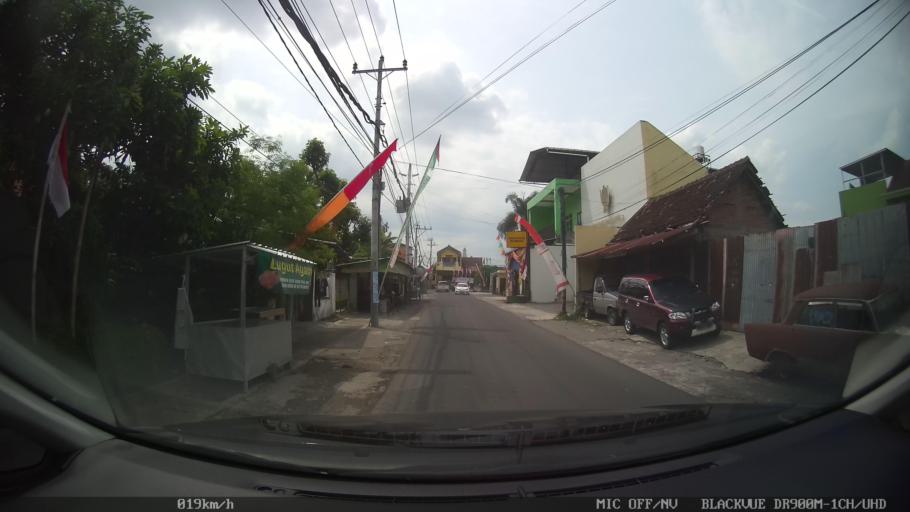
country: ID
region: Daerah Istimewa Yogyakarta
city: Yogyakarta
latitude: -7.7975
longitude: 110.4024
